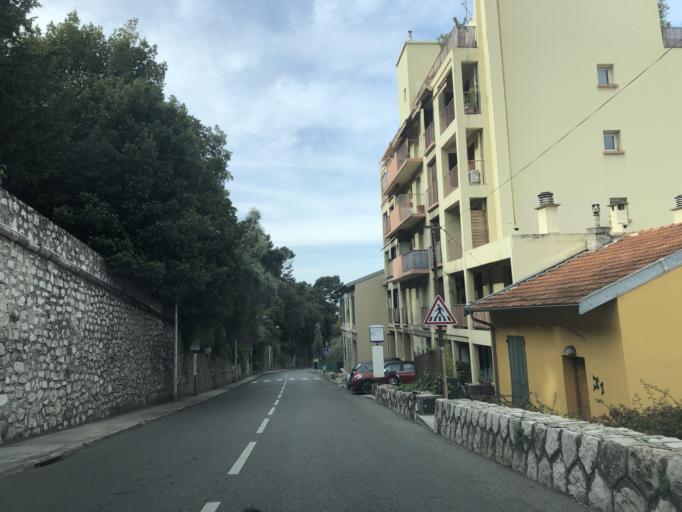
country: FR
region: Provence-Alpes-Cote d'Azur
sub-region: Departement des Alpes-Maritimes
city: Villefranche-sur-Mer
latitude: 43.7101
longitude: 7.2946
